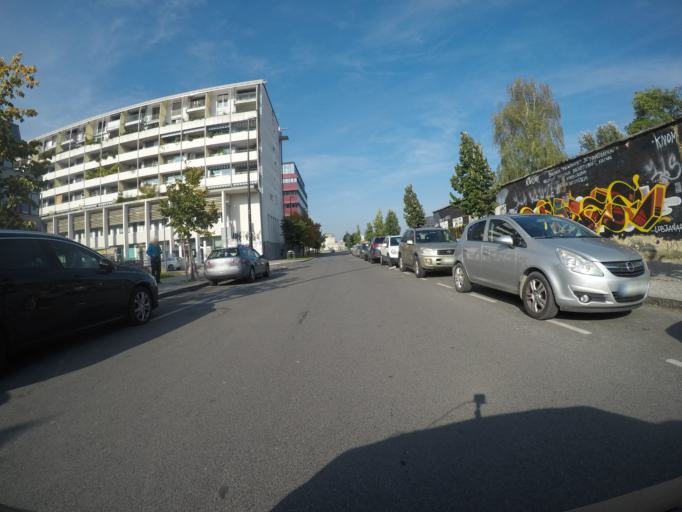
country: SI
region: Ljubljana
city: Ljubljana
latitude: 46.0565
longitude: 14.5155
